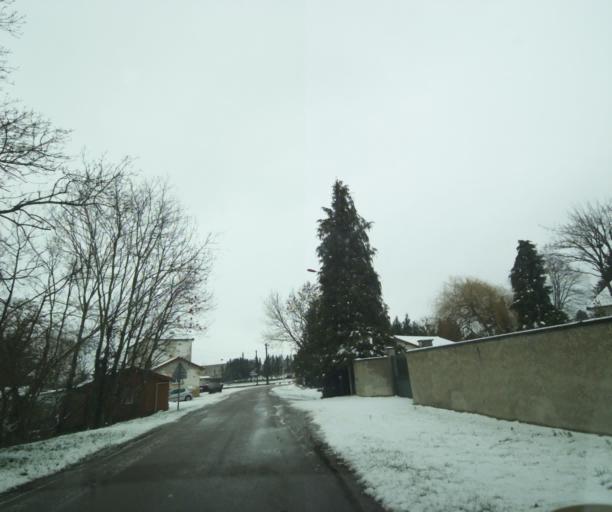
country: FR
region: Champagne-Ardenne
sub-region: Departement de la Haute-Marne
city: Laneuville-a-Remy
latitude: 48.4088
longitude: 4.8466
